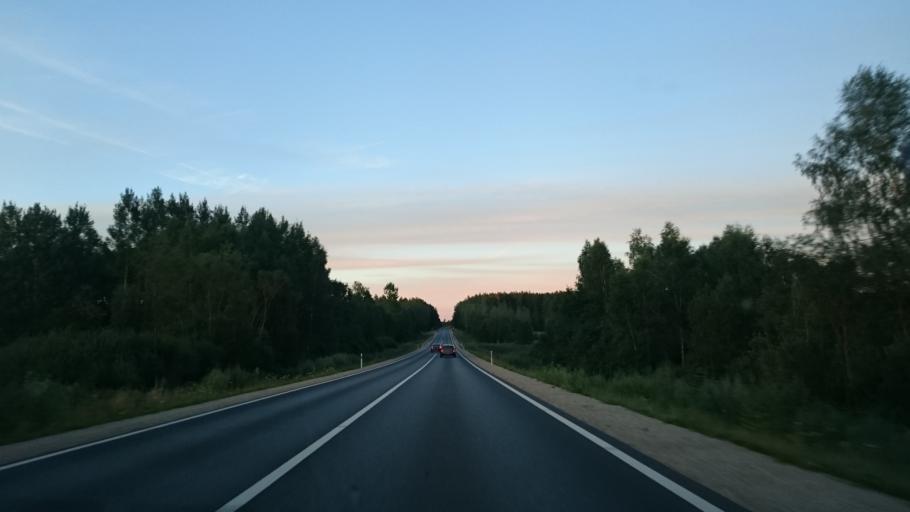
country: LV
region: Jaunpils
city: Jaunpils
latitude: 56.6928
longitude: 23.1322
